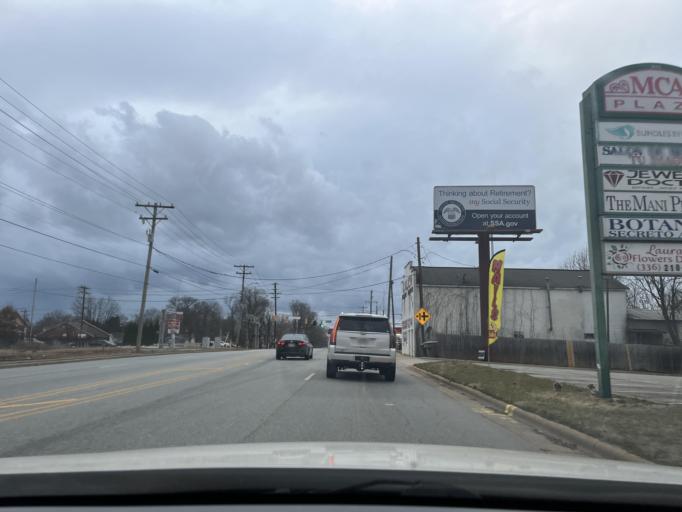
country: US
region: North Carolina
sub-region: Guilford County
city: Greensboro
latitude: 36.0608
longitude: -79.8541
